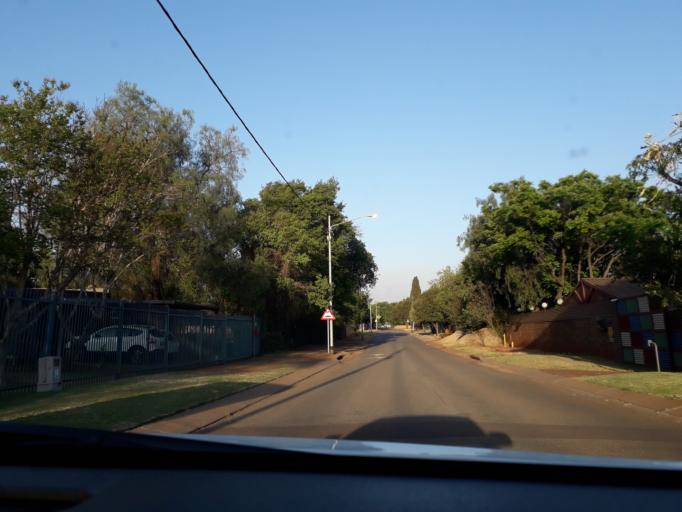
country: ZA
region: Gauteng
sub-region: City of Tshwane Metropolitan Municipality
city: Centurion
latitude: -25.8619
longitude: 28.2000
